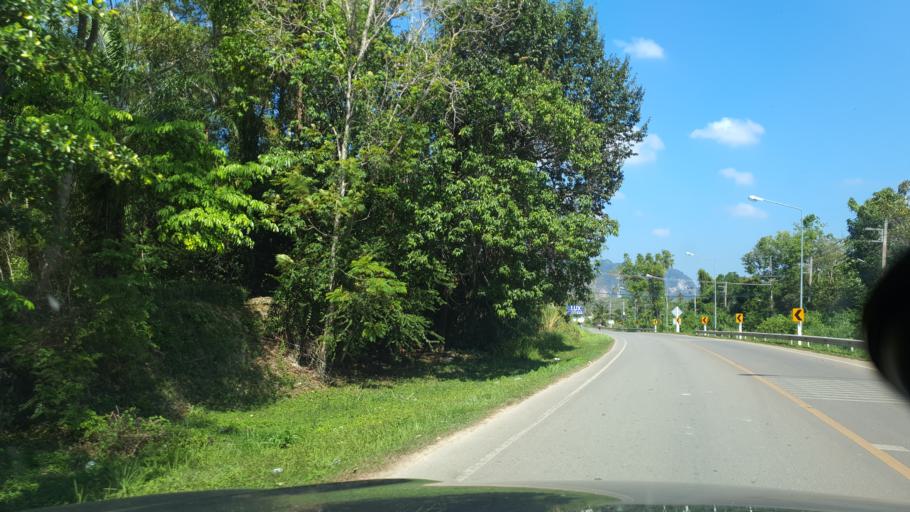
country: TH
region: Phangnga
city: Ban Ao Nang
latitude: 8.0435
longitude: 98.8612
